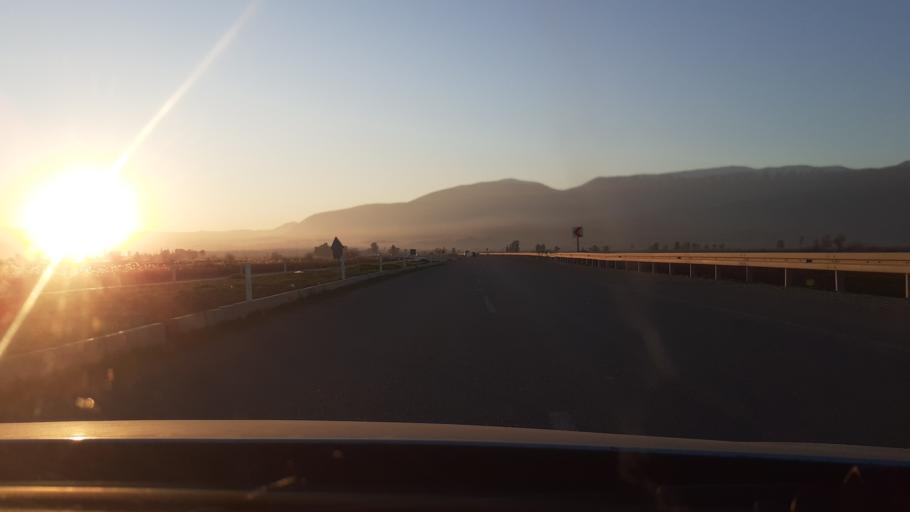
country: TR
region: Hatay
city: Kirikhan
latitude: 36.5069
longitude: 36.4333
